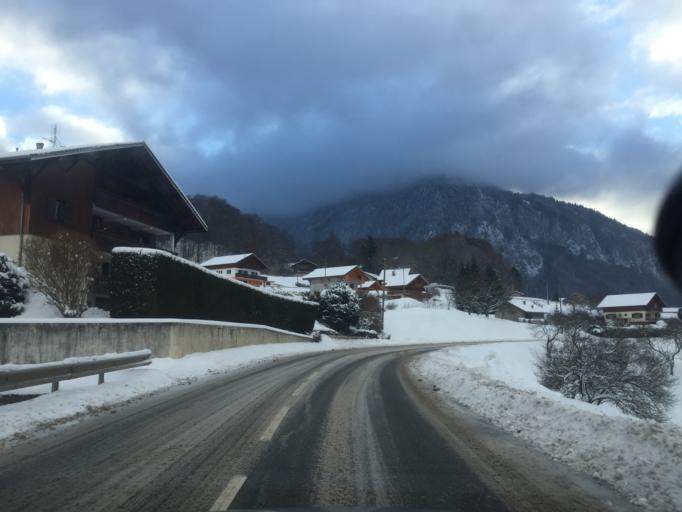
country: FR
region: Rhone-Alpes
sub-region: Departement de la Haute-Savoie
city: Abondance
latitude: 46.3201
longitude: 6.6738
